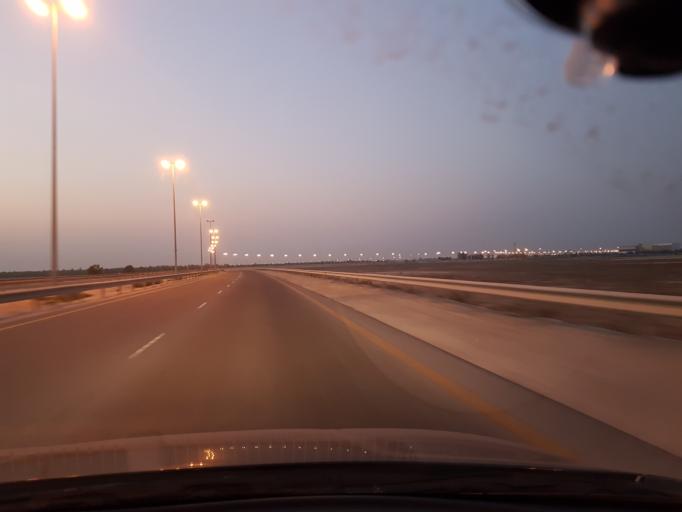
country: BH
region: Central Governorate
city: Dar Kulayb
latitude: 26.0063
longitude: 50.4849
